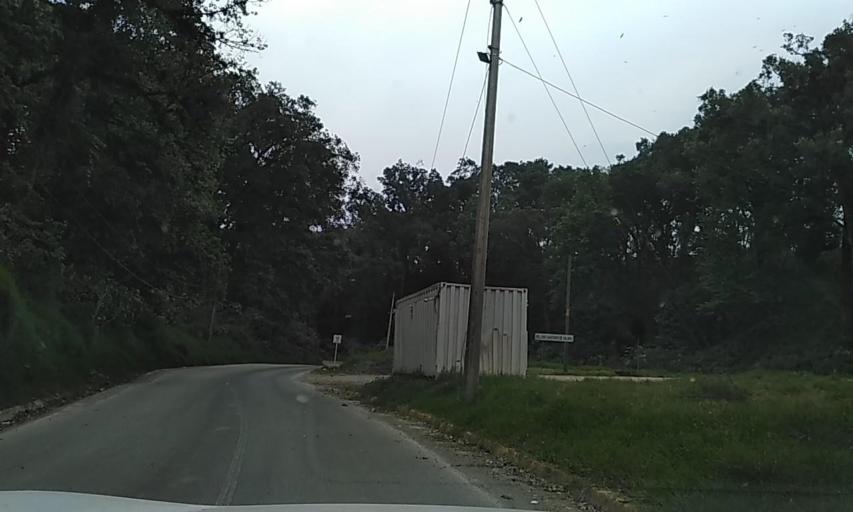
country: MX
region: Veracruz
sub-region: Jilotepec
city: El Pueblito (Garbanzal)
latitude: 19.5768
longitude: -96.8931
